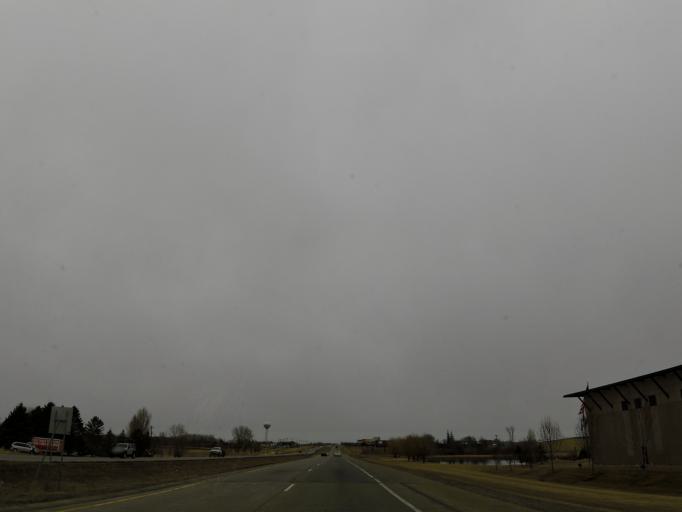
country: US
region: Minnesota
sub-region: Le Sueur County
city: Le Sueur
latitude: 44.4936
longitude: -93.8725
